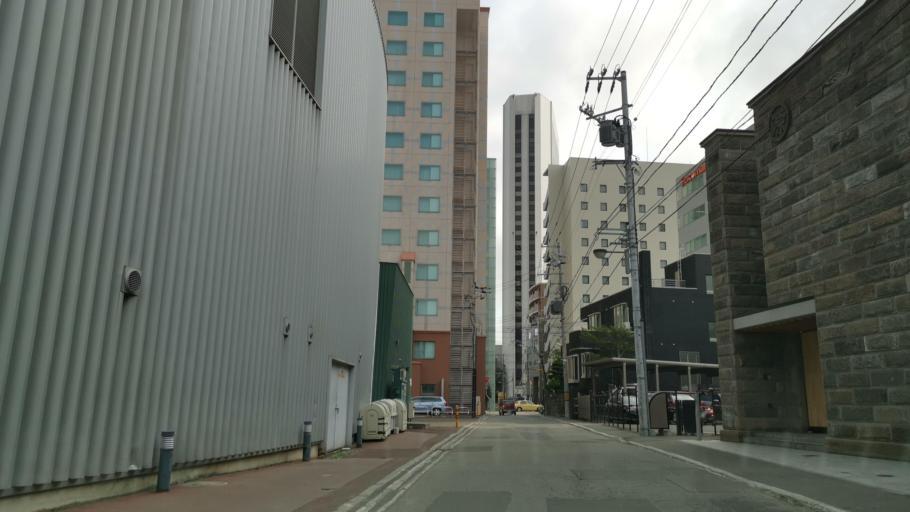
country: JP
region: Hokkaido
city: Sapporo
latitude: 43.0494
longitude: 141.3531
